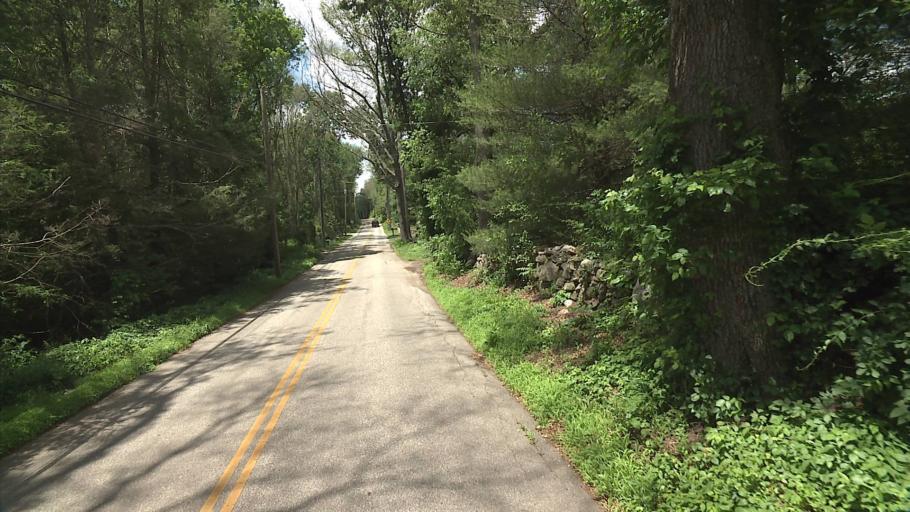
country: US
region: Connecticut
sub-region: New London County
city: Old Mystic
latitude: 41.4428
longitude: -71.8948
